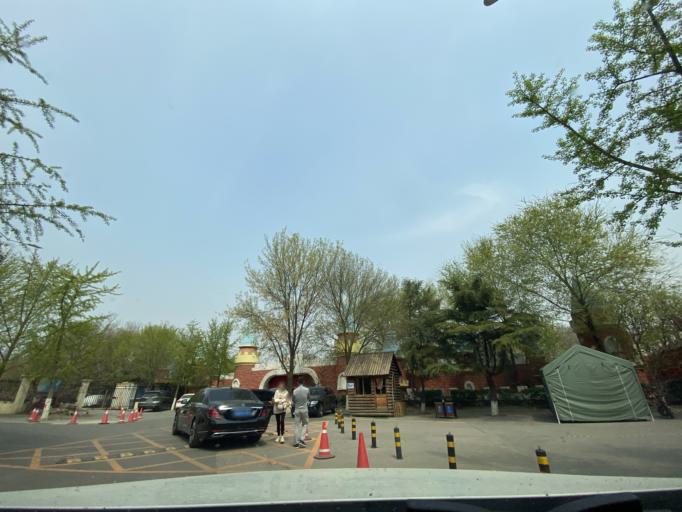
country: CN
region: Beijing
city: Sijiqing
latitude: 39.9427
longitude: 116.2459
